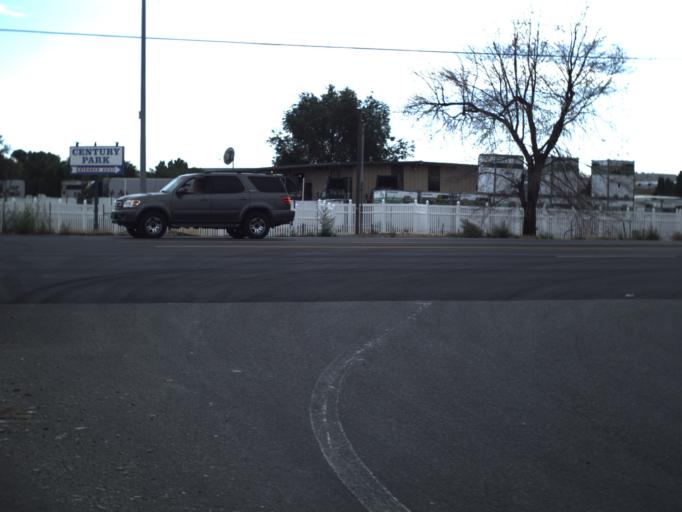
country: US
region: Utah
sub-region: Weber County
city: Marriott-Slaterville
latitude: 41.2289
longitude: -112.0142
